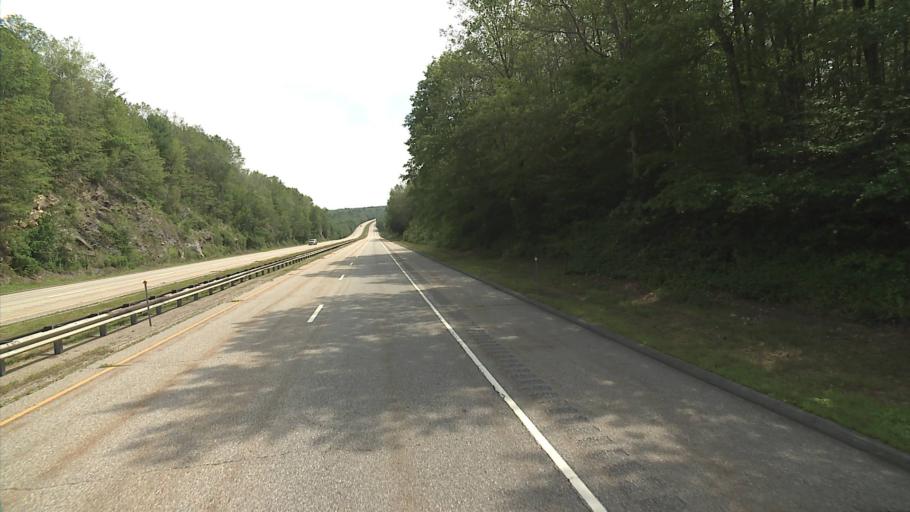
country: US
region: Connecticut
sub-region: Windham County
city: Danielson
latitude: 41.7737
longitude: -71.8528
